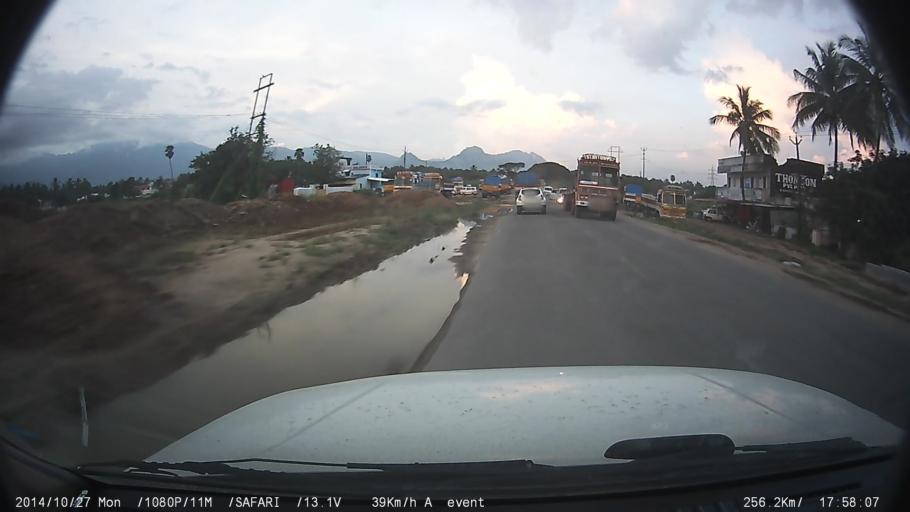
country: IN
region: Kerala
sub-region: Palakkad district
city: Palakkad
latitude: 10.7629
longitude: 76.6735
